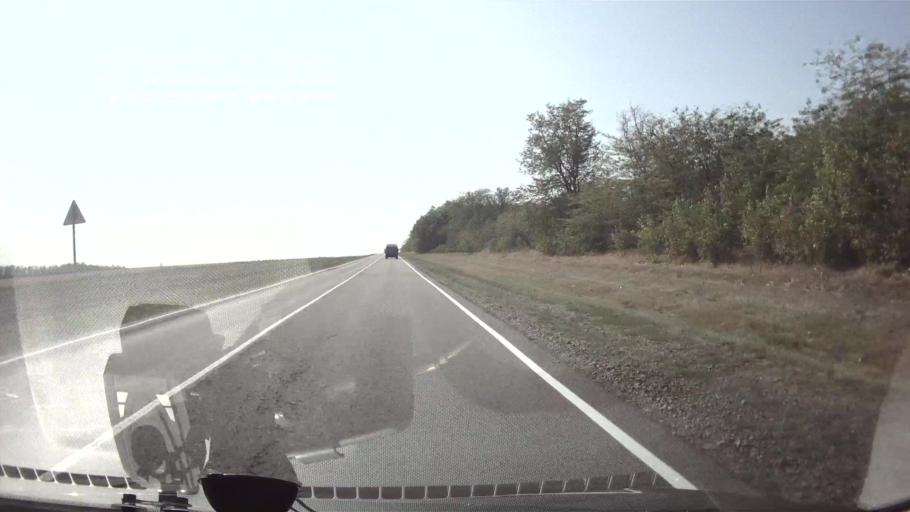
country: RU
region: Krasnodarskiy
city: Novopokrovskaya
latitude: 45.8342
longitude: 40.7202
